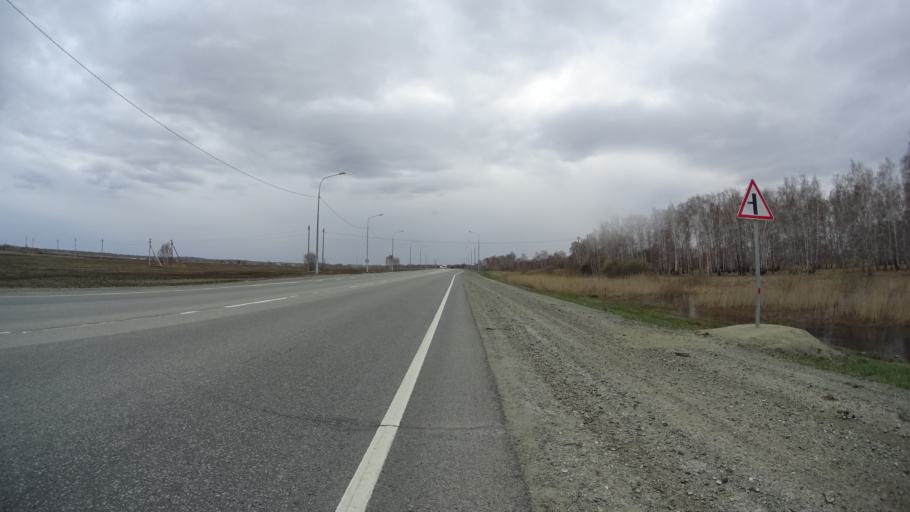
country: RU
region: Chelyabinsk
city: Krasnogorskiy
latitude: 54.6859
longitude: 61.2477
